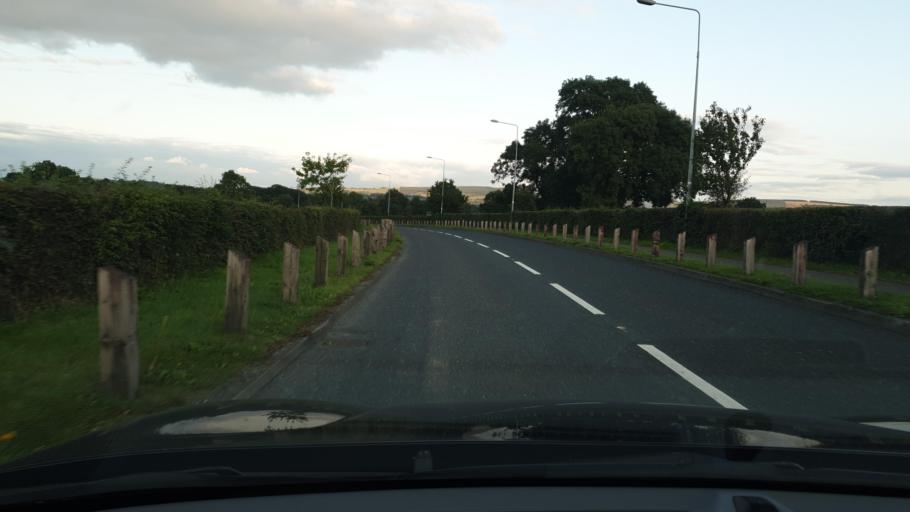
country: IE
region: Leinster
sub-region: Kildare
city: Kill
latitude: 53.2515
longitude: -6.5738
